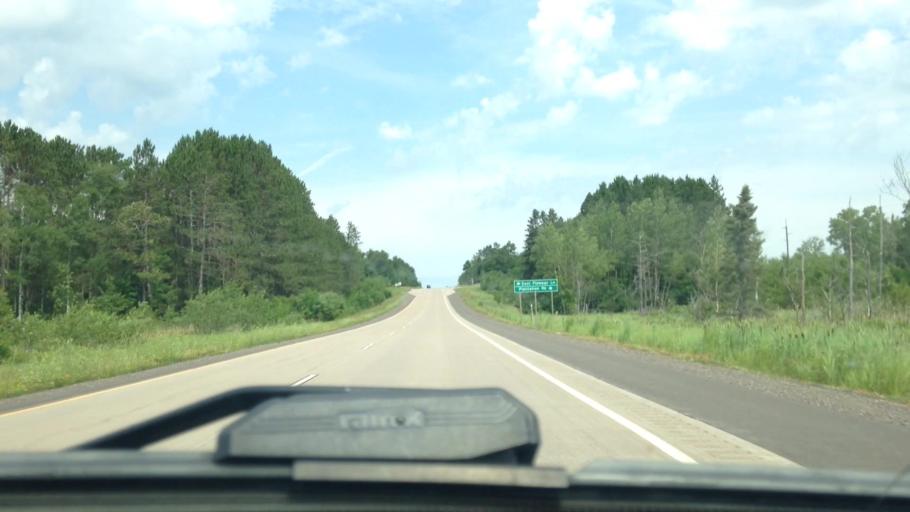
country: US
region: Wisconsin
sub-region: Douglas County
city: Lake Nebagamon
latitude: 46.2704
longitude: -91.8038
